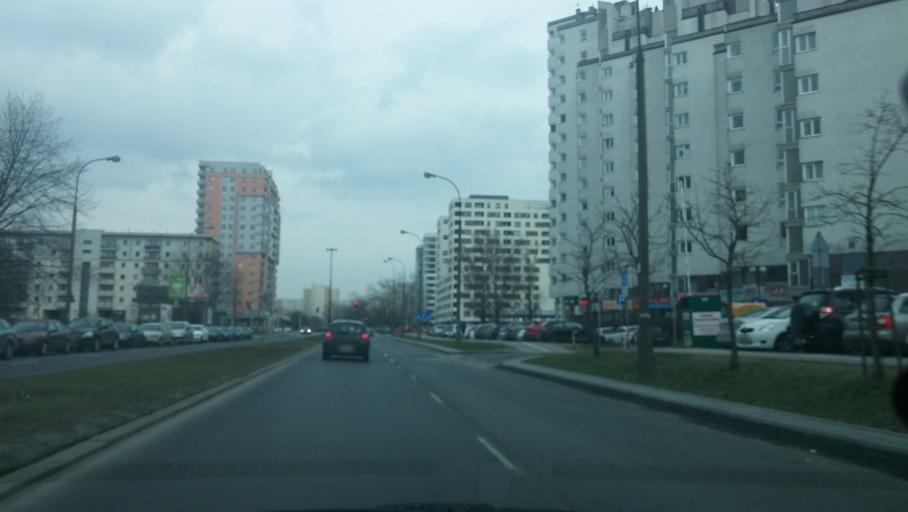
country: PL
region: Masovian Voivodeship
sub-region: Warszawa
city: Praga Poludnie
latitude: 52.2224
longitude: 21.0886
